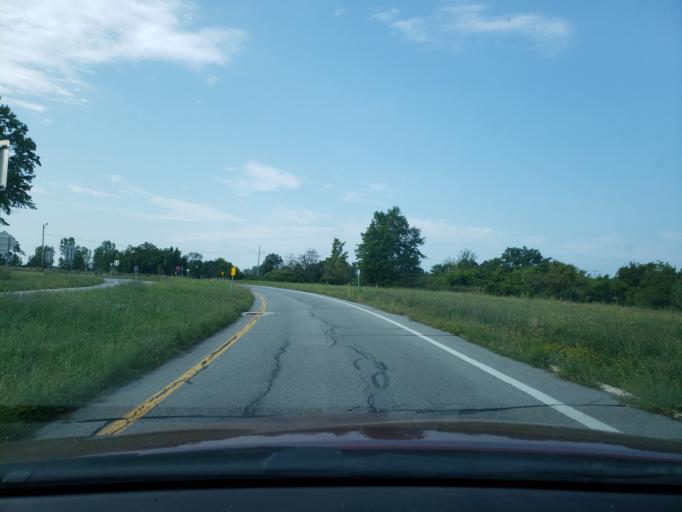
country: US
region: New York
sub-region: Monroe County
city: Greece
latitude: 43.2812
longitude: -77.6934
